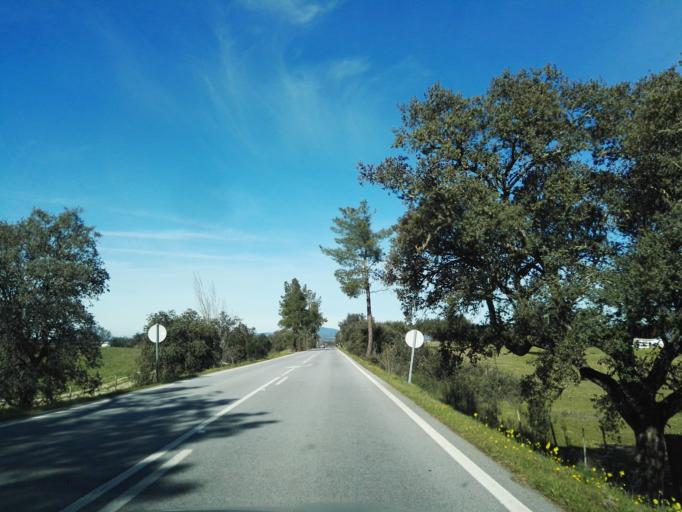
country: PT
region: Portalegre
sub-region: Arronches
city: Arronches
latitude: 39.0808
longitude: -7.2811
